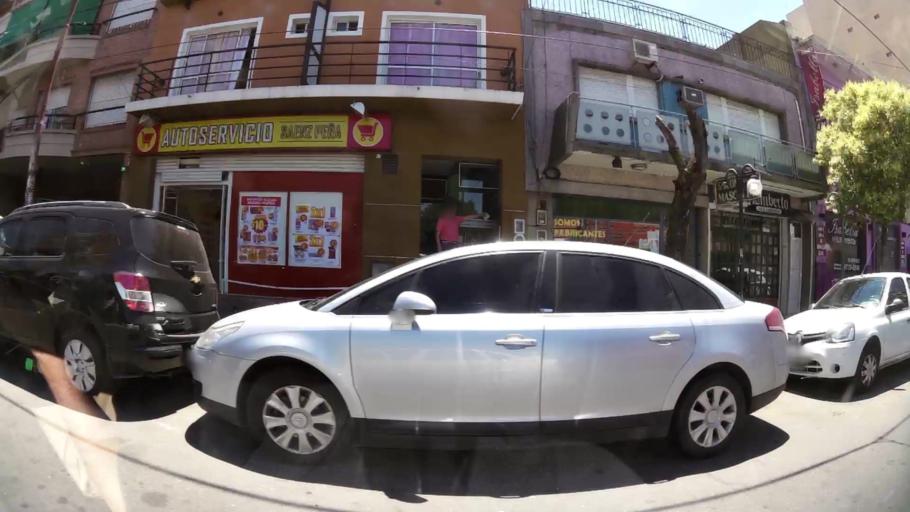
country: AR
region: Buenos Aires
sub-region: Partido de General San Martin
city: General San Martin
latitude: -34.6017
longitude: -58.5273
